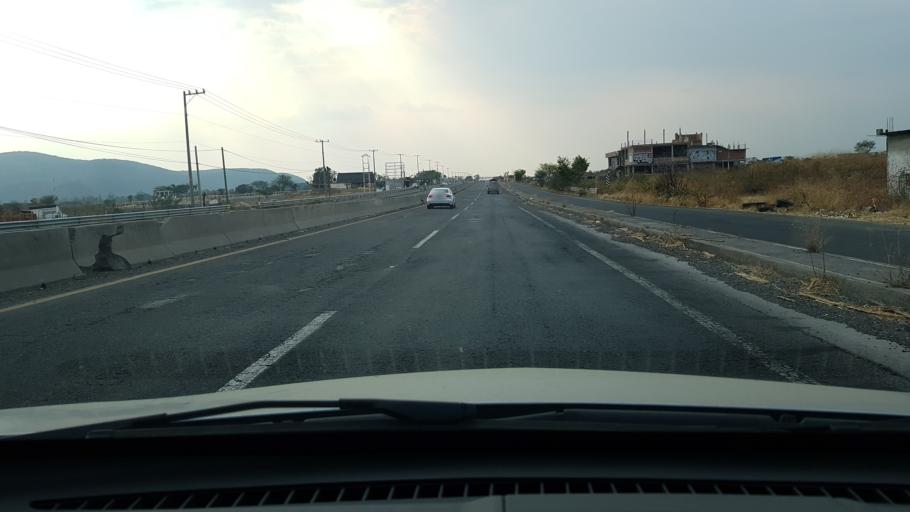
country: MX
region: Morelos
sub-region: Ayala
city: Unidad Habitacional Mariano Matamoros
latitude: 18.7387
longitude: -98.8271
